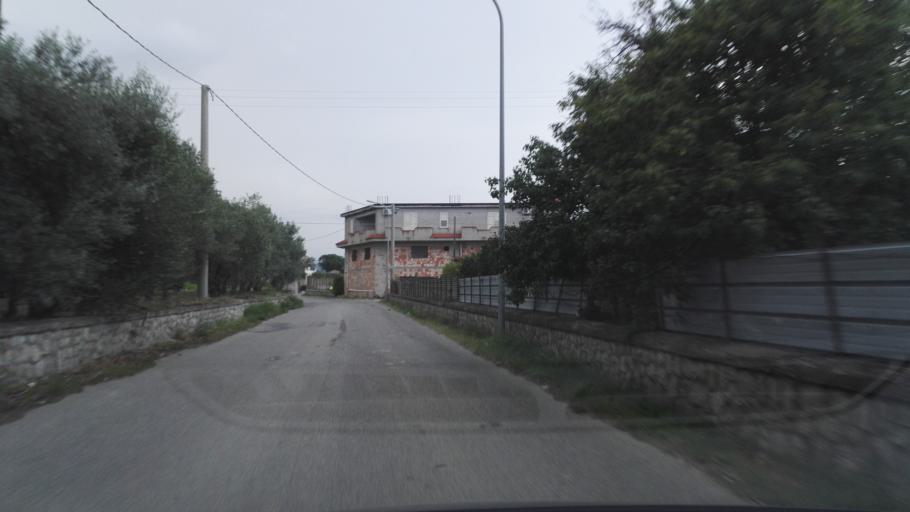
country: IT
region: Calabria
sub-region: Provincia di Reggio Calabria
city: Caulonia Marina
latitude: 38.3599
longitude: 16.4695
